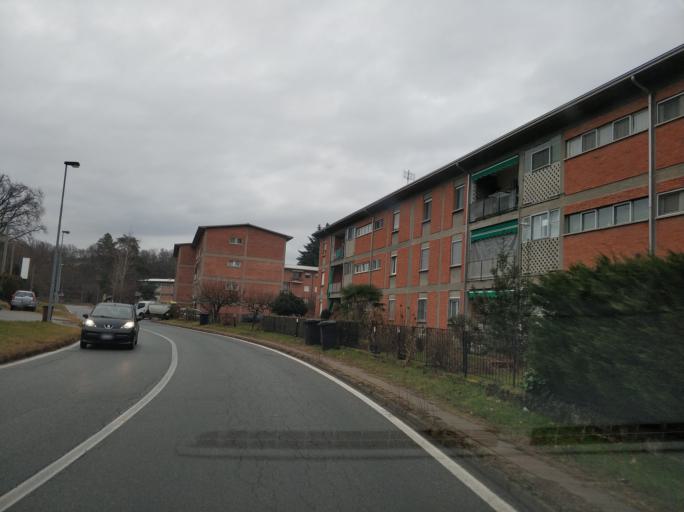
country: IT
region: Piedmont
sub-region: Provincia di Torino
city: Pavone Canavese
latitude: 45.4432
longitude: 7.8680
